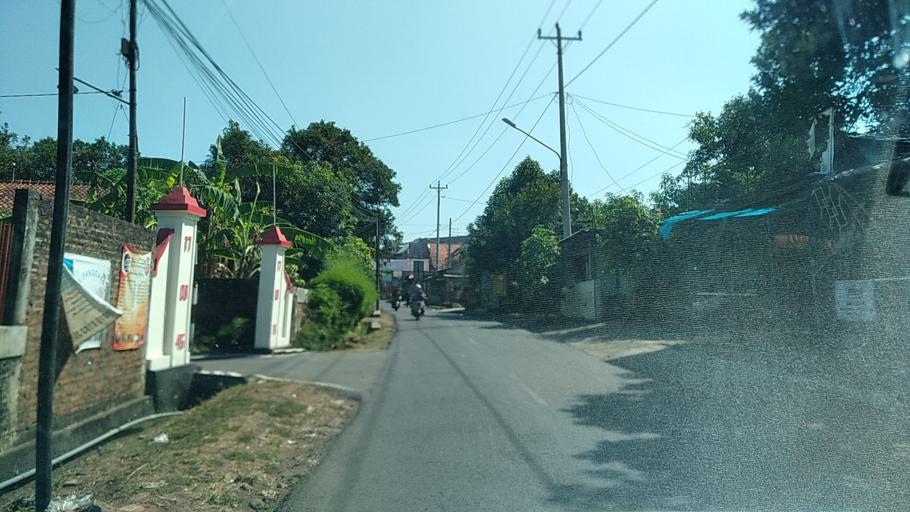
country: ID
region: Central Java
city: Semarang
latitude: -7.0649
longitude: 110.4408
